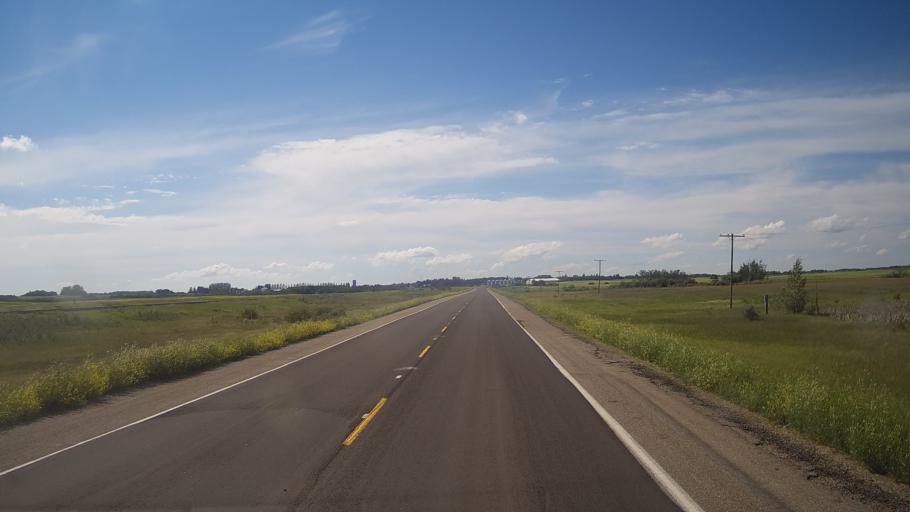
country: CA
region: Saskatchewan
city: Foam Lake
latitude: 51.2529
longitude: -103.7086
